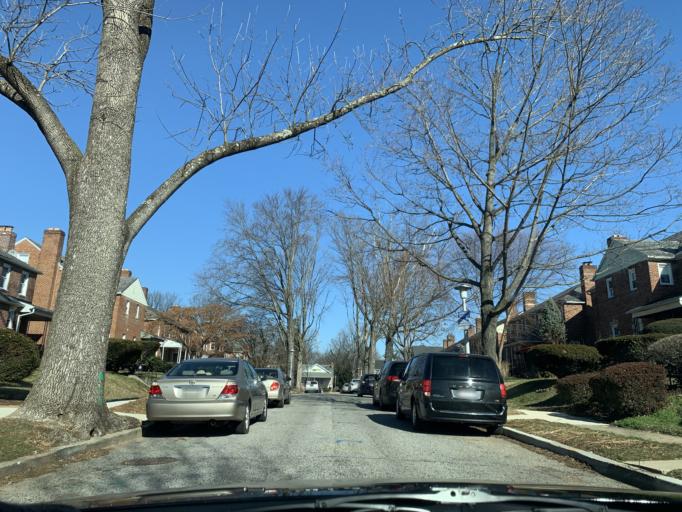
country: US
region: Maryland
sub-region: Baltimore County
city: Lochearn
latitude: 39.3273
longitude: -76.6713
